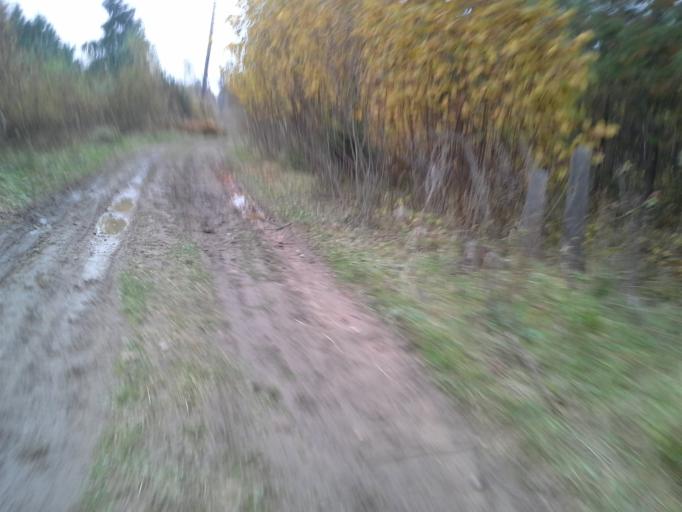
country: RU
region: Moskovskaya
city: Nazar'yevo
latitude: 55.6928
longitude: 37.0110
